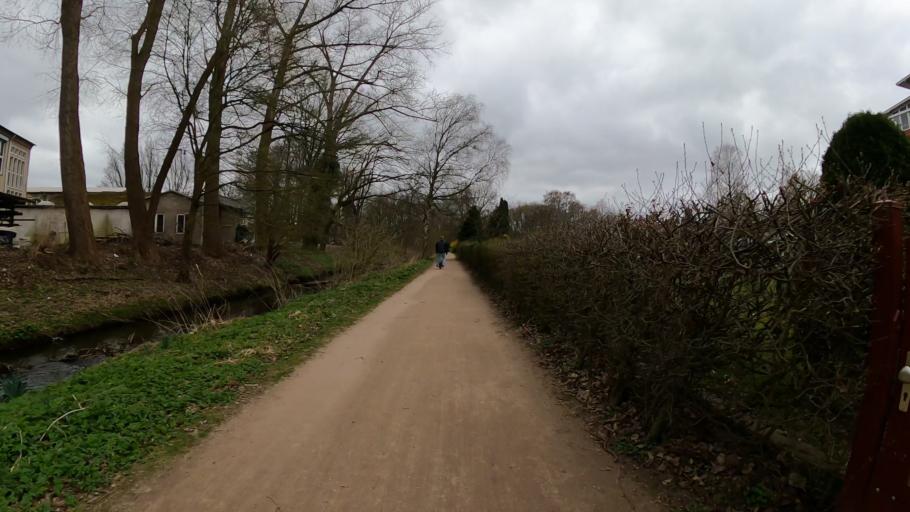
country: DE
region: Hamburg
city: Hamburg-Nord
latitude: 53.6119
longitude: 9.9665
